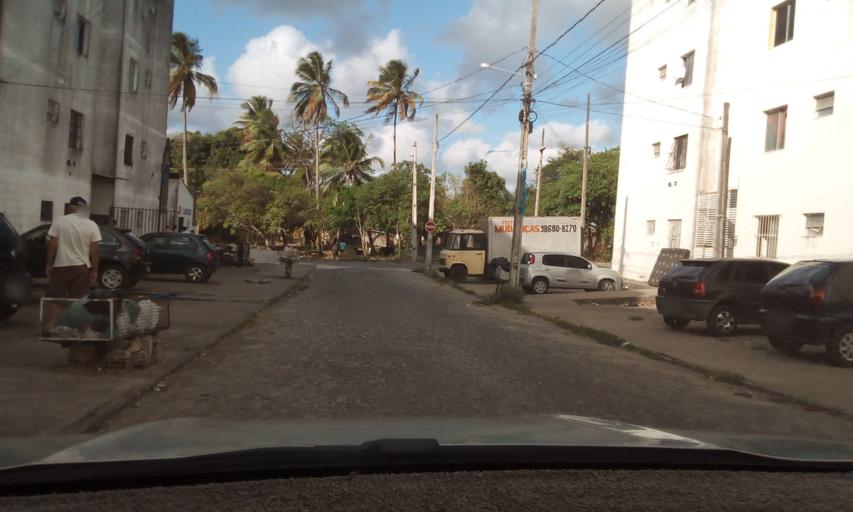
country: BR
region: Paraiba
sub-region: Bayeux
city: Bayeux
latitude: -7.1684
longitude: -34.9155
